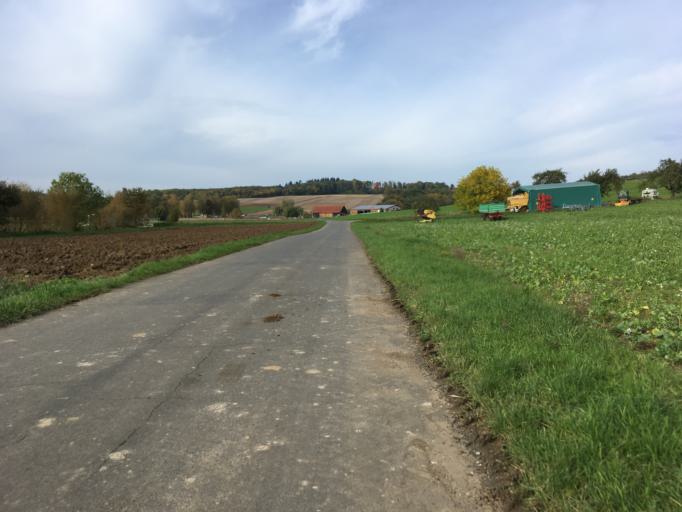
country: DE
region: Baden-Wuerttemberg
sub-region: Karlsruhe Region
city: Rosenberg
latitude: 49.4844
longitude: 9.4643
